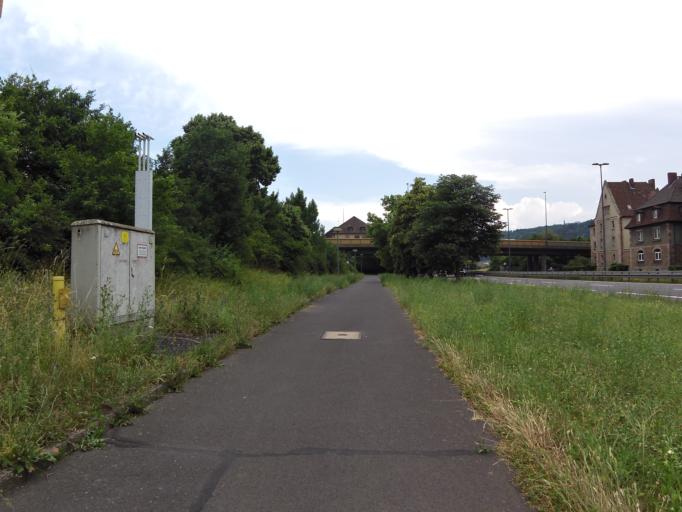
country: DE
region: Bavaria
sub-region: Regierungsbezirk Unterfranken
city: Zell am Main
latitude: 49.8087
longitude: 9.8843
